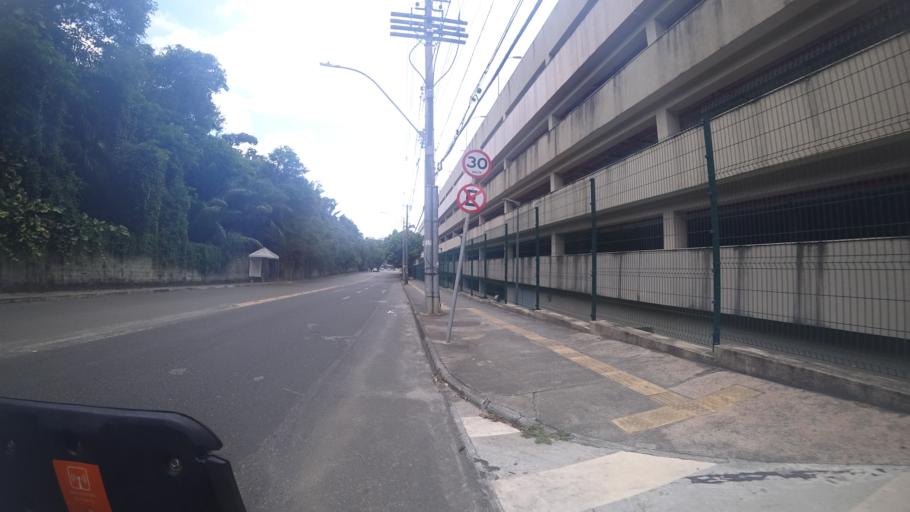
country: BR
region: Bahia
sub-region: Salvador
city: Salvador
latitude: -12.9988
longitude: -38.4690
